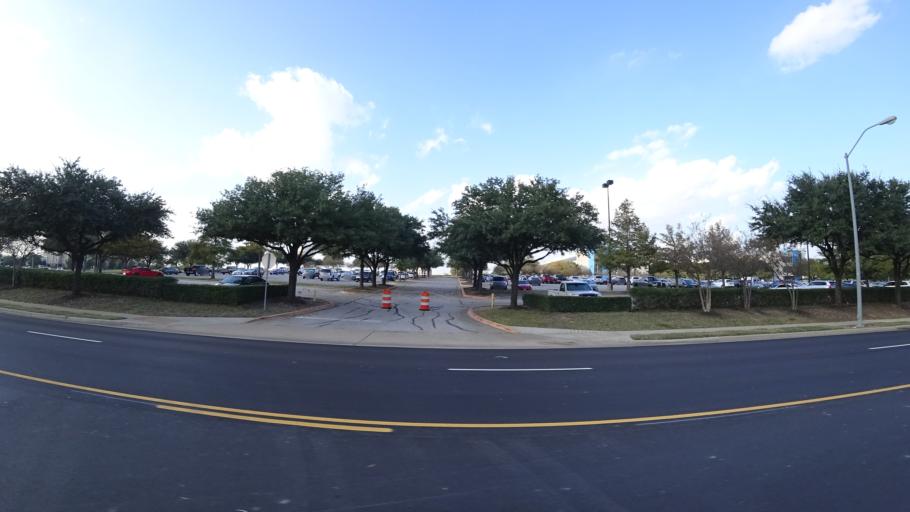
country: US
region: Texas
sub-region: Williamson County
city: Round Rock
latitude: 30.4861
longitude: -97.6712
